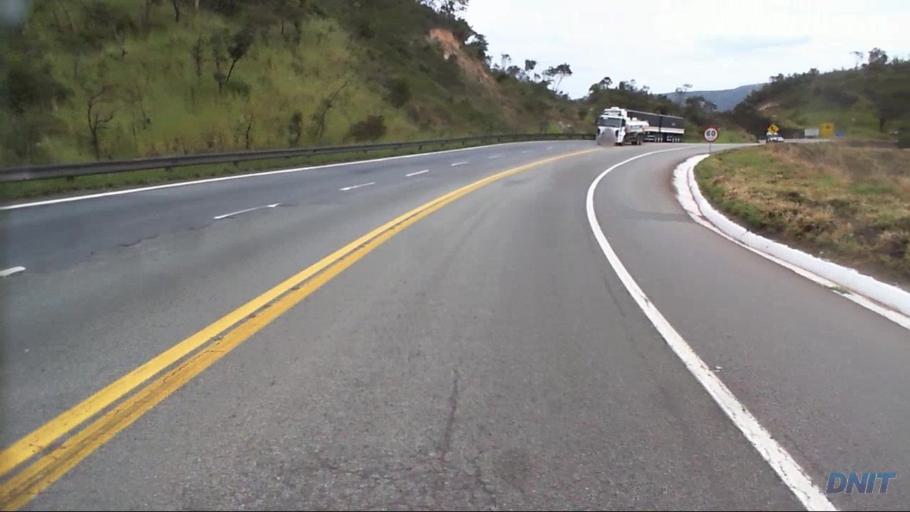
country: BR
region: Minas Gerais
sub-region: Caete
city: Caete
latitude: -19.7865
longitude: -43.7141
